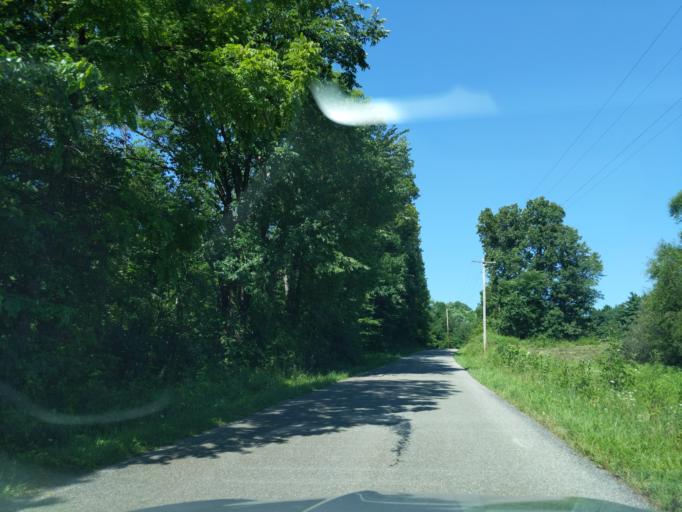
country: US
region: Indiana
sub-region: Decatur County
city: Westport
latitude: 39.1117
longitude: -85.4517
